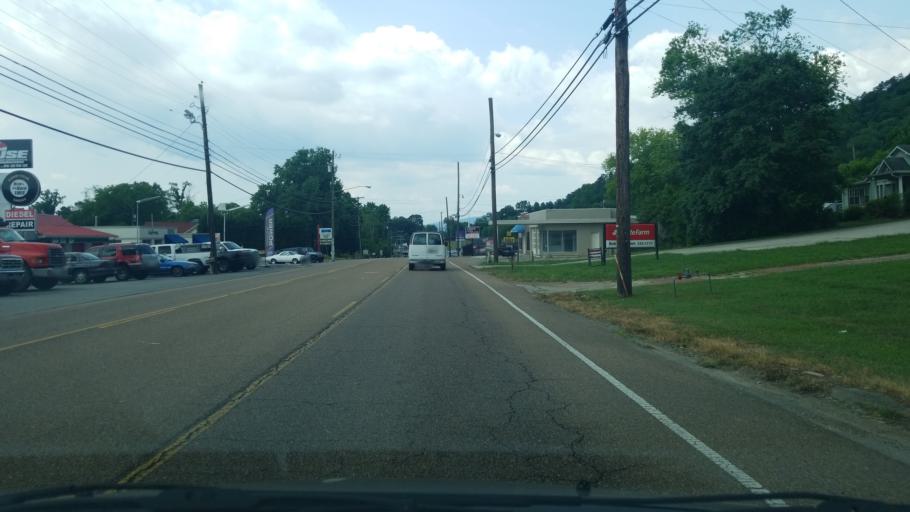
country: US
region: Tennessee
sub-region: Hamilton County
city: Soddy-Daisy
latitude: 35.2441
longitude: -85.1903
